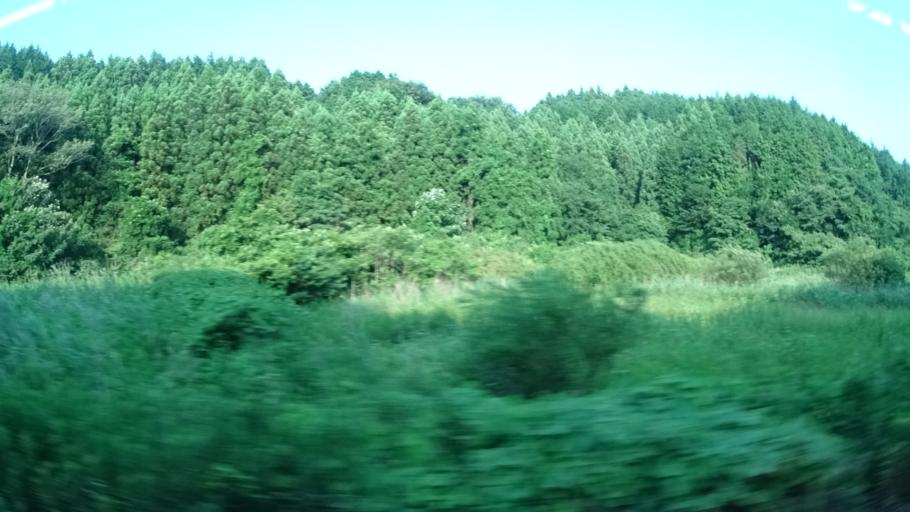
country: JP
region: Ibaraki
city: Takahagi
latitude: 36.7358
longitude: 140.7195
